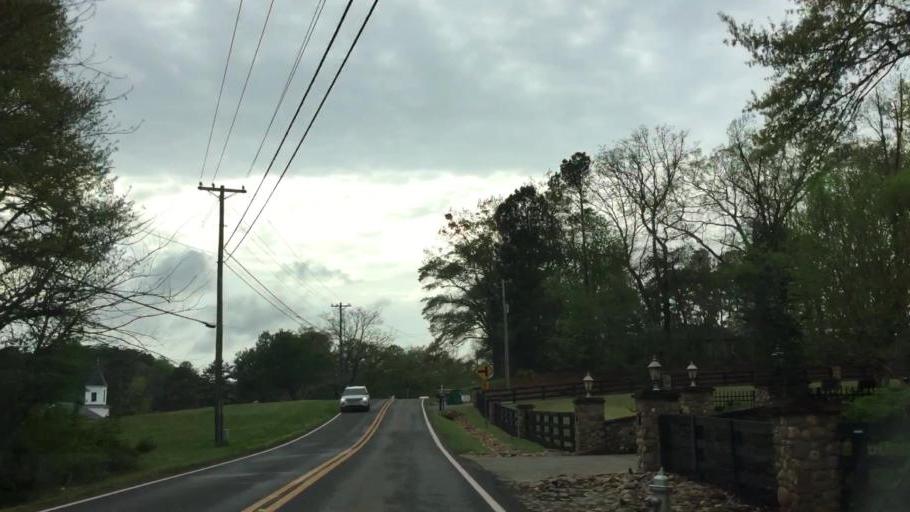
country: US
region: Georgia
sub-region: Fulton County
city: Milton
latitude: 34.1980
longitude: -84.3568
